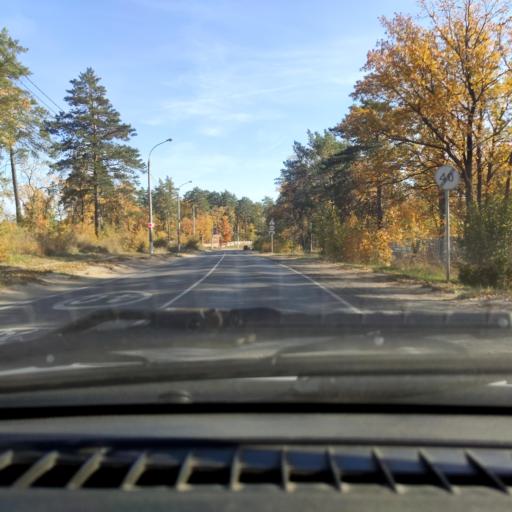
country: RU
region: Samara
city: Tol'yatti
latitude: 53.4865
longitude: 49.3118
